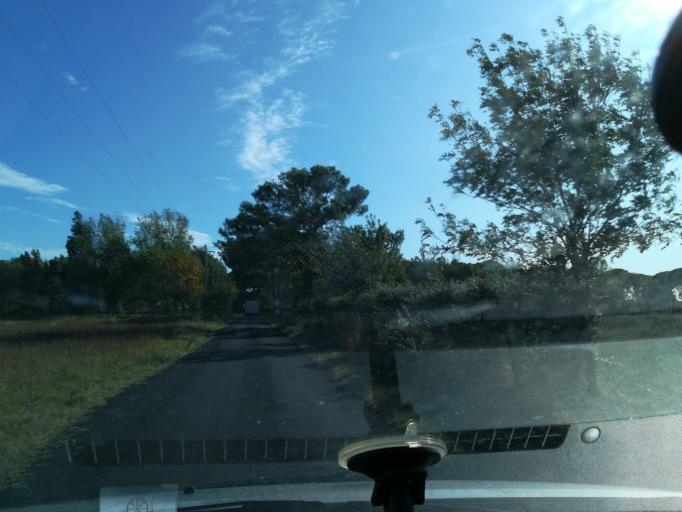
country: FR
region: Languedoc-Roussillon
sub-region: Departement de l'Herault
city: Portiragnes
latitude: 43.2887
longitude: 3.3731
